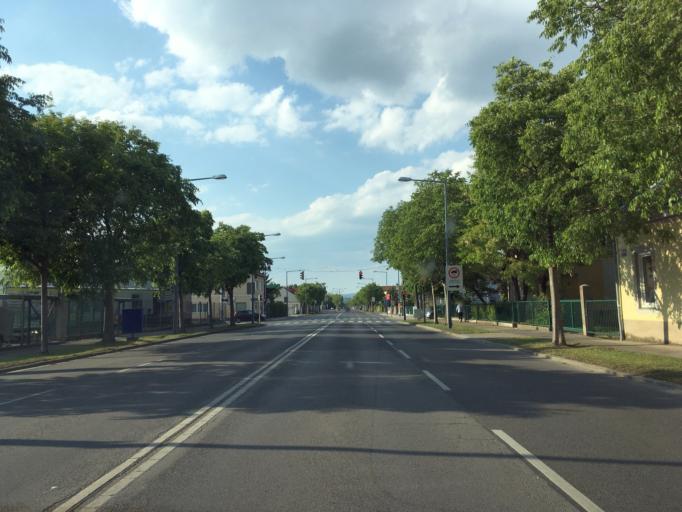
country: AT
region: Lower Austria
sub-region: Politischer Bezirk Modling
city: Vosendorf
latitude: 48.1406
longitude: 16.3241
